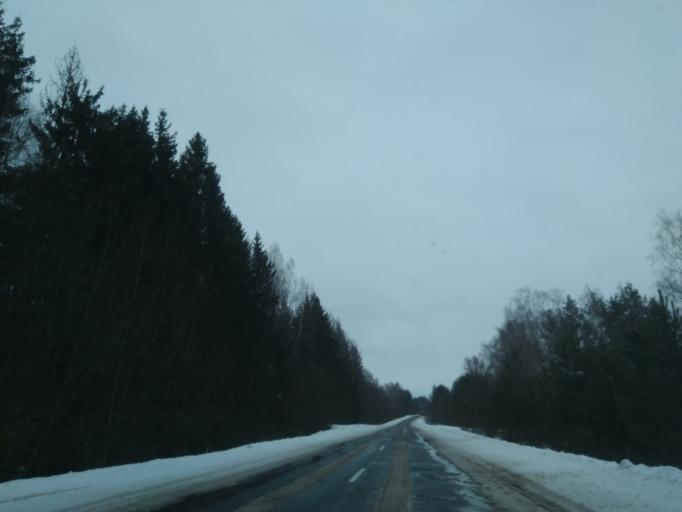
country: BY
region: Minsk
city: Ivyanyets
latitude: 53.8480
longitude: 26.7907
